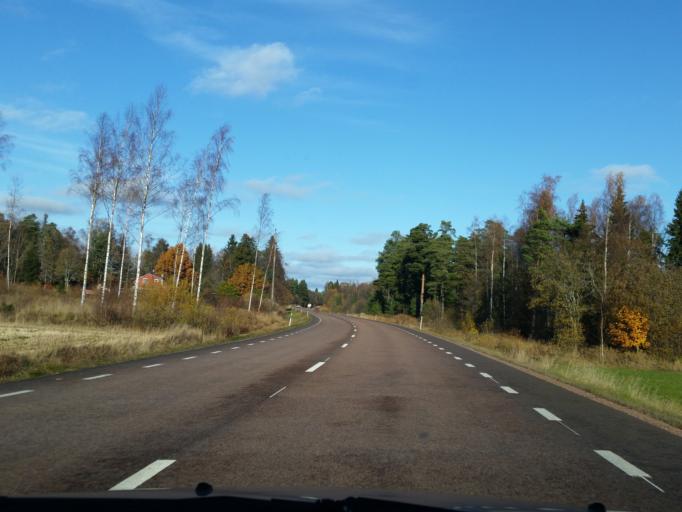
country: AX
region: Alands landsbygd
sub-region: Finstroem
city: Finstroem
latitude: 60.2183
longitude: 19.9822
